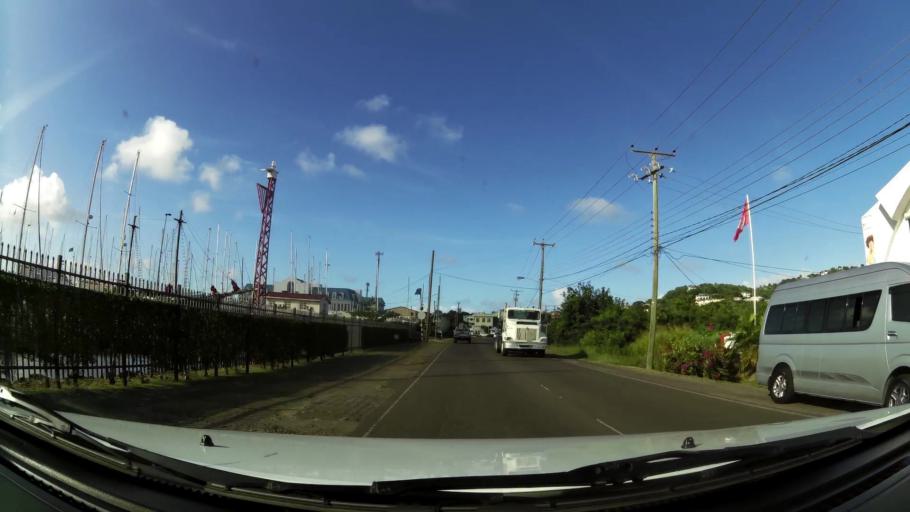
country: LC
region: Gros-Islet
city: Gros Islet
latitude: 14.0776
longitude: -60.9478
